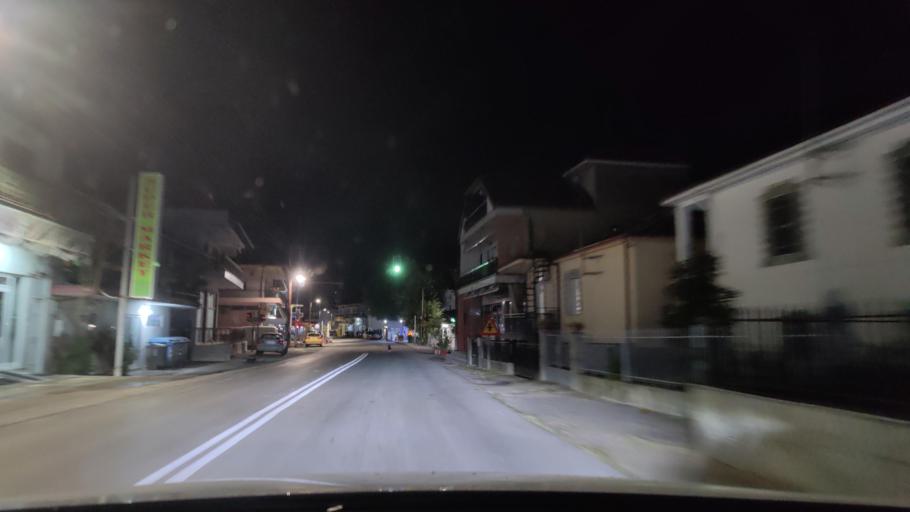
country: GR
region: Central Macedonia
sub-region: Nomos Serron
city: Neo Petritsi
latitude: 41.2652
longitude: 23.2512
